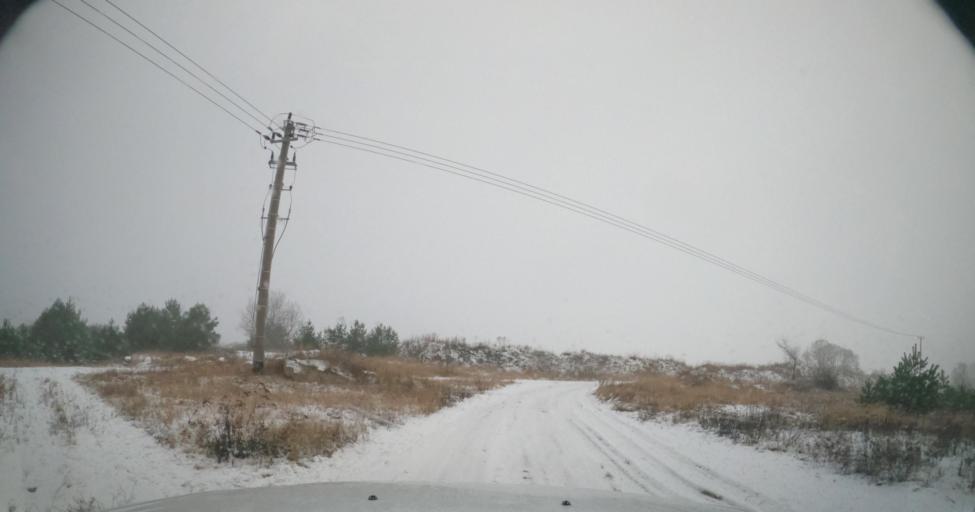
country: PL
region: West Pomeranian Voivodeship
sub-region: Powiat kamienski
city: Golczewo
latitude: 53.7821
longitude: 14.9563
